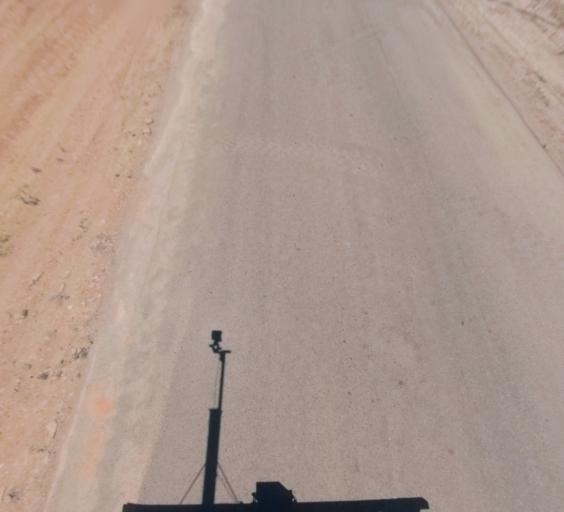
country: US
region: California
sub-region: Madera County
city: Bonadelle Ranchos-Madera Ranchos
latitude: 36.9279
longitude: -119.8307
